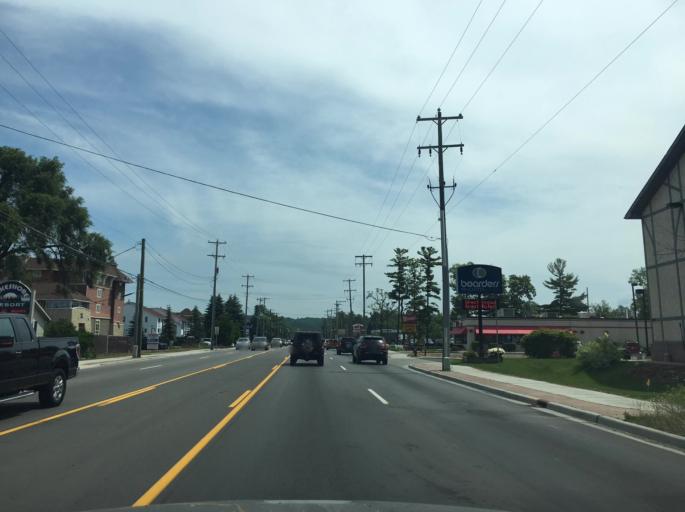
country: US
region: Michigan
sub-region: Grand Traverse County
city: Traverse City
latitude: 44.7457
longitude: -85.5392
